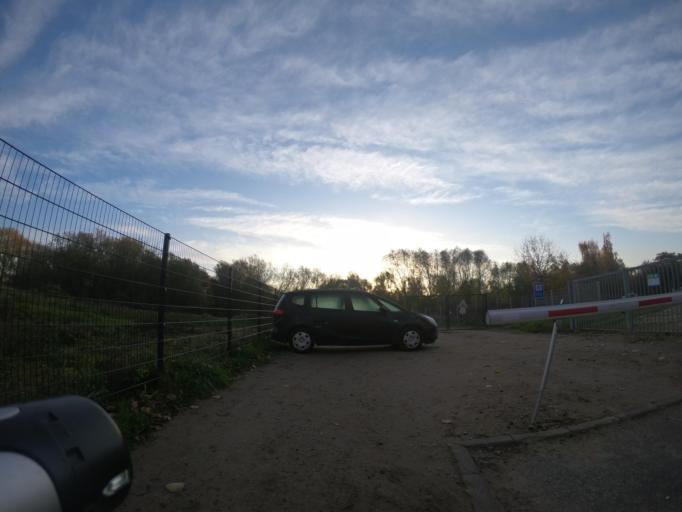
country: DE
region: Mecklenburg-Vorpommern
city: Rostock
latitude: 54.0786
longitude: 12.1455
